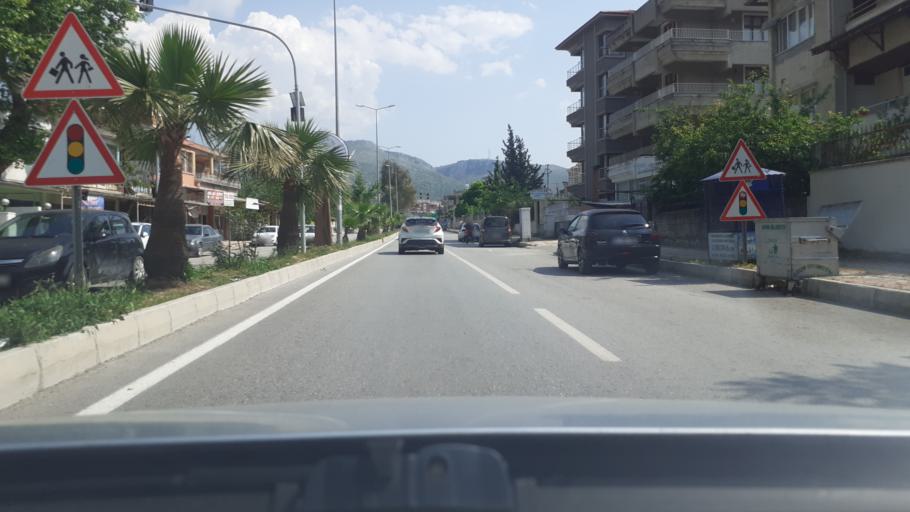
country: TR
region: Hatay
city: Harbiye
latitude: 36.1416
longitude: 36.1415
